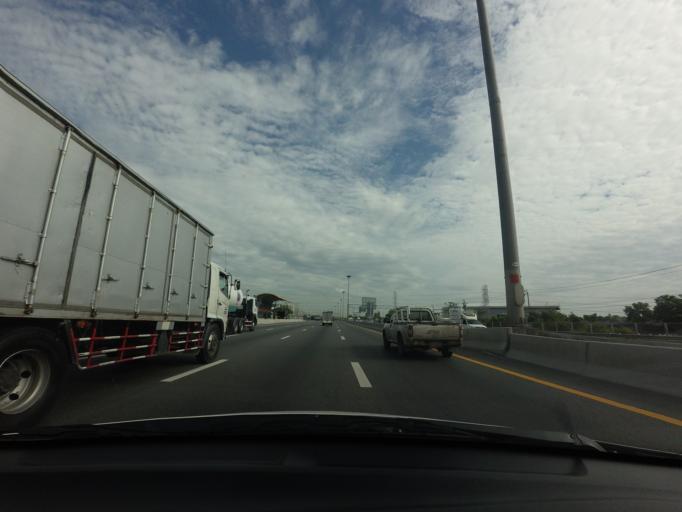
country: TH
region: Pathum Thani
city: Lam Luk Ka
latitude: 13.9147
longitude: 100.7021
